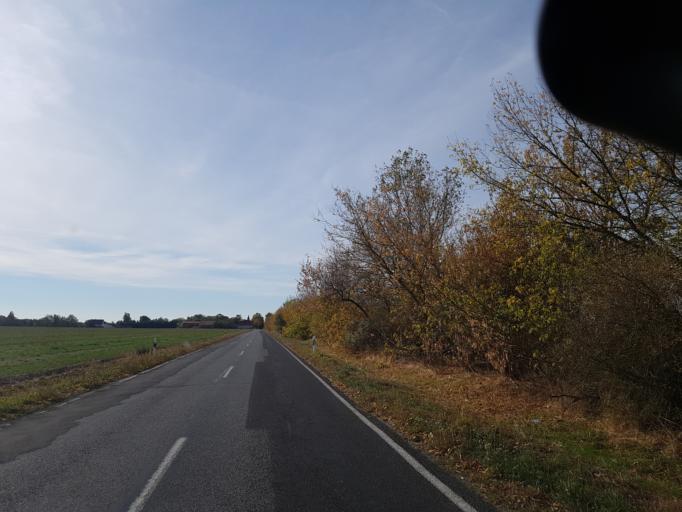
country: DE
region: Brandenburg
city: Ihlow
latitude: 51.9131
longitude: 13.2239
